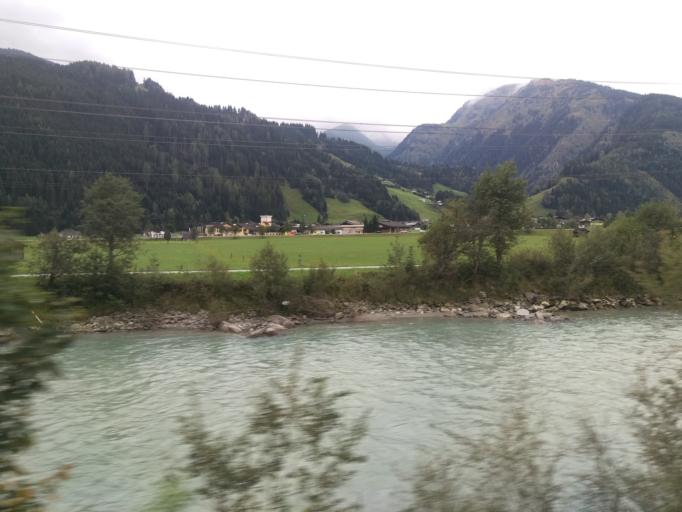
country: AT
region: Salzburg
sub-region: Politischer Bezirk Zell am See
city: Hollersbach im Pinzgau
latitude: 47.2791
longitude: 12.4287
